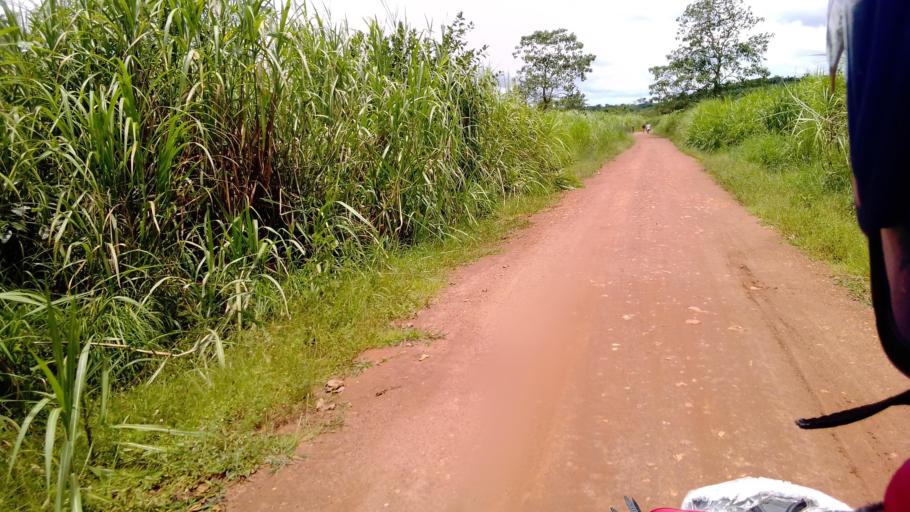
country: SL
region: Eastern Province
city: Koidu
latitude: 8.6752
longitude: -10.9357
